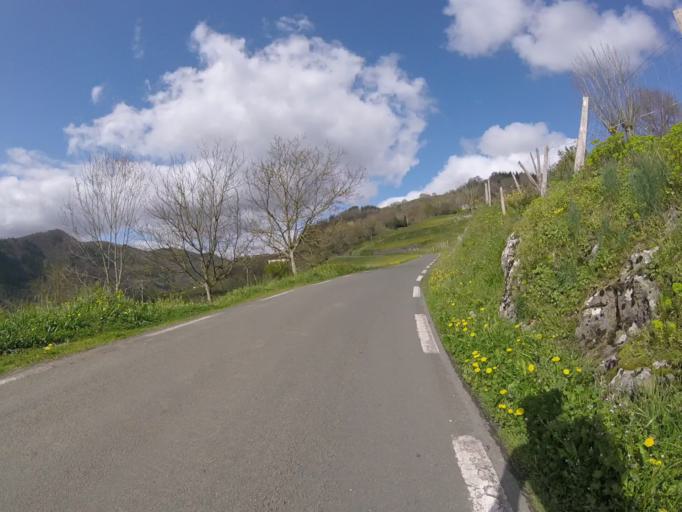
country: ES
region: Basque Country
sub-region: Provincia de Guipuzcoa
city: Tolosa
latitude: 43.1280
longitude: -2.0972
